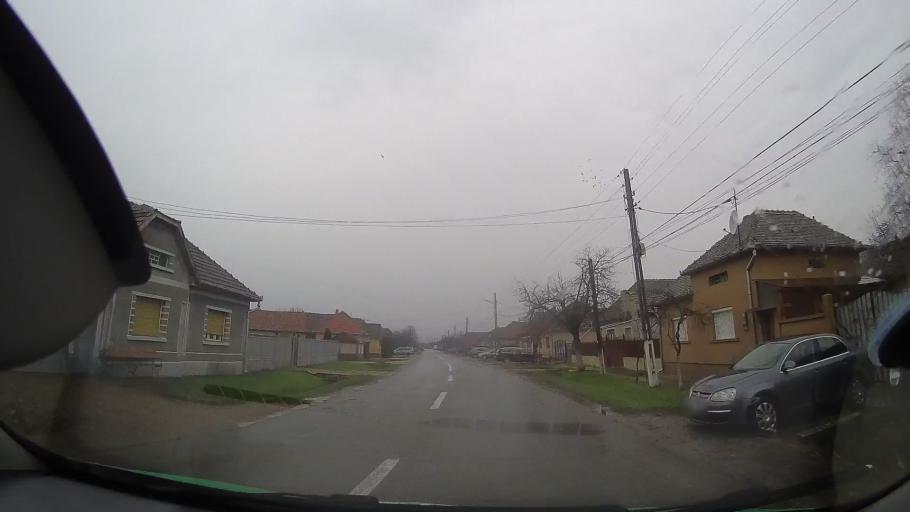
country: RO
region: Bihor
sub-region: Comuna Tulca
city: Tulca
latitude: 46.7919
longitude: 21.7699
